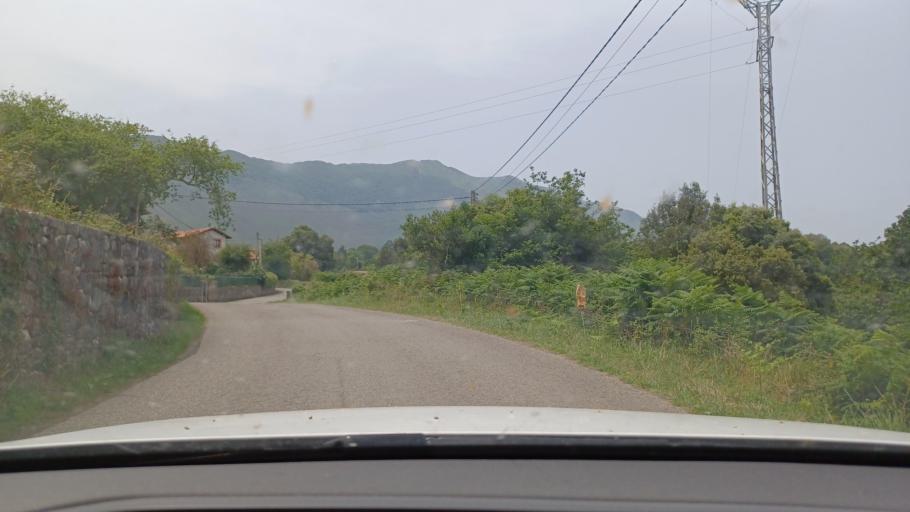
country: ES
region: Asturias
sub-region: Province of Asturias
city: Ribadesella
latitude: 43.4456
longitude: -4.9815
